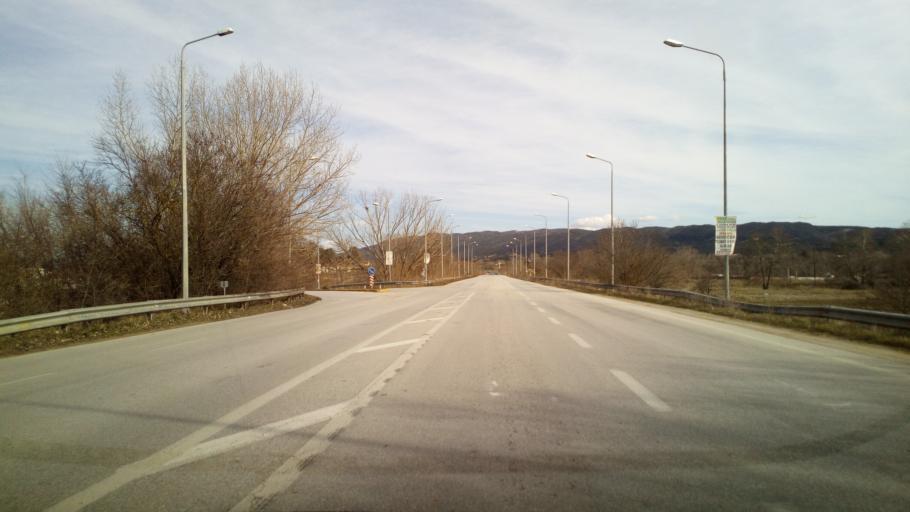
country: GR
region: Central Macedonia
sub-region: Nomos Thessalonikis
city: Gerakarou
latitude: 40.6329
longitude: 23.2401
